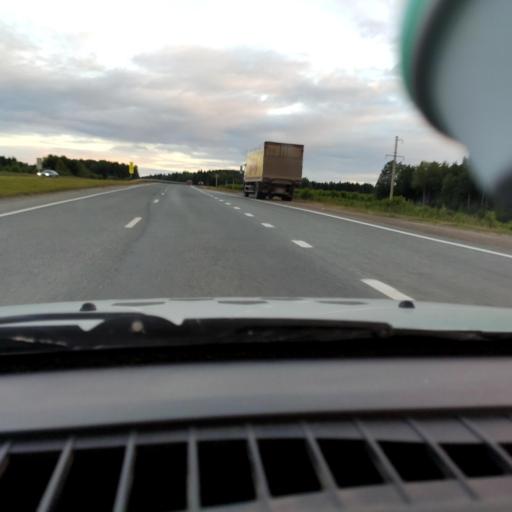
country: RU
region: Perm
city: Polazna
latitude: 58.2660
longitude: 56.4120
